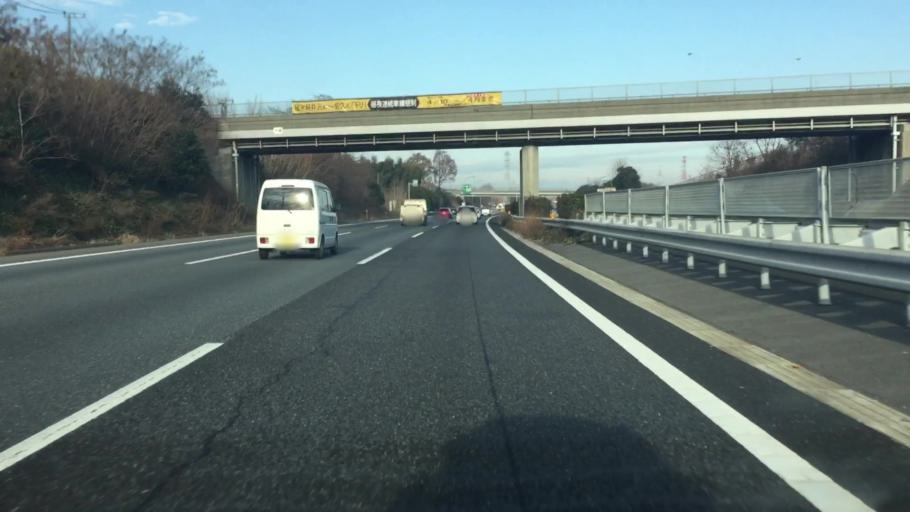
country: JP
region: Saitama
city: Yorii
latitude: 36.1680
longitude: 139.1980
